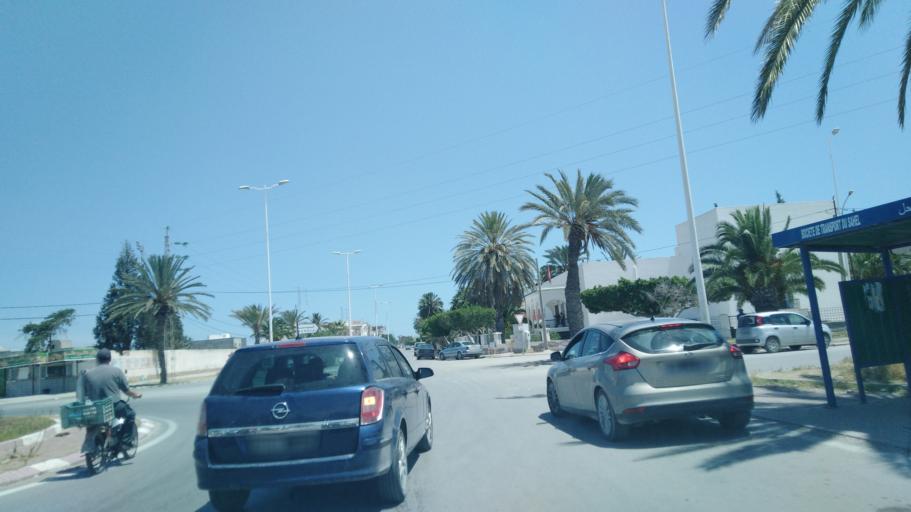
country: TN
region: Al Mahdiyah
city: Ksour Essaf
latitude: 35.4237
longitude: 10.9978
